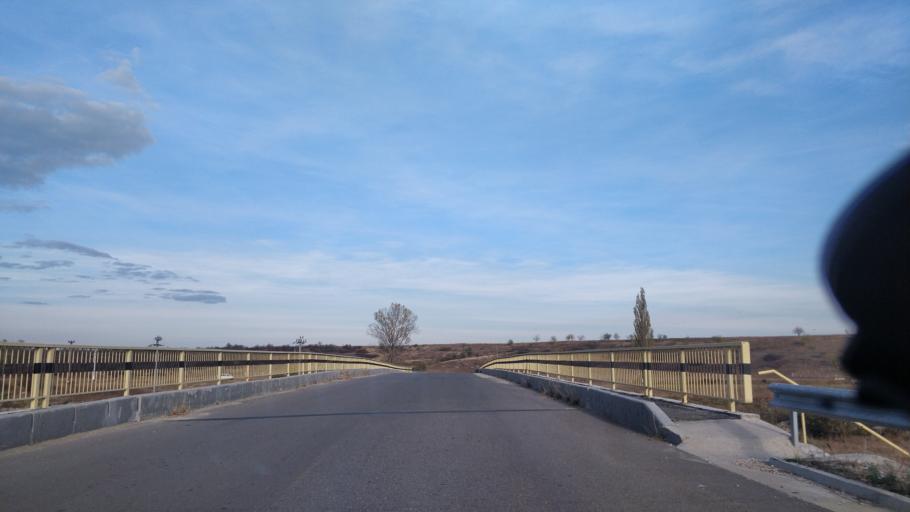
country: RO
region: Giurgiu
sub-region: Comuna Bucsani
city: Bucsani
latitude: 44.3577
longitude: 25.6664
